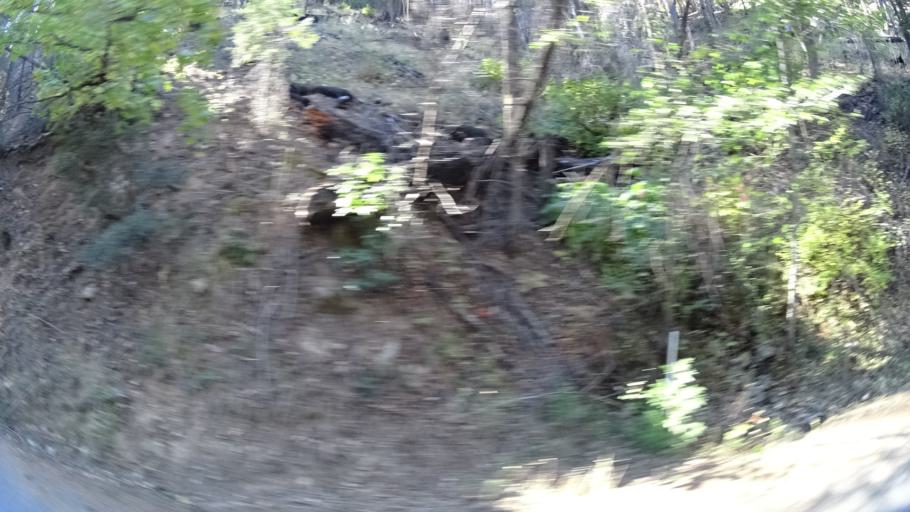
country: US
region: California
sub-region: Siskiyou County
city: Happy Camp
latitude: 41.3346
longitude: -123.0485
